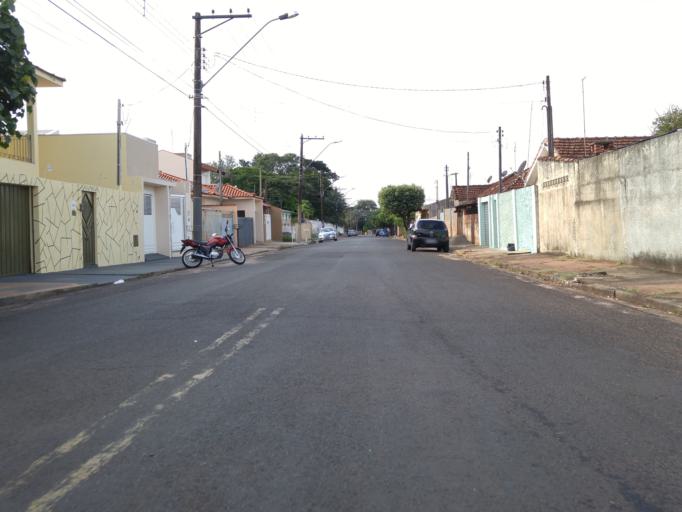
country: BR
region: Sao Paulo
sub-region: Paraguacu Paulista
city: Paraguacu Paulista
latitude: -22.4094
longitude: -50.5757
